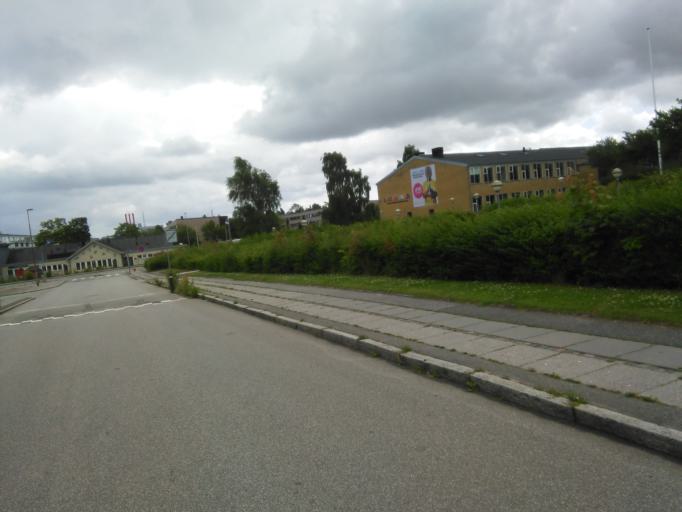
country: DK
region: Central Jutland
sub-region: Arhus Kommune
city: Stavtrup
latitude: 56.1123
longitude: 10.1492
